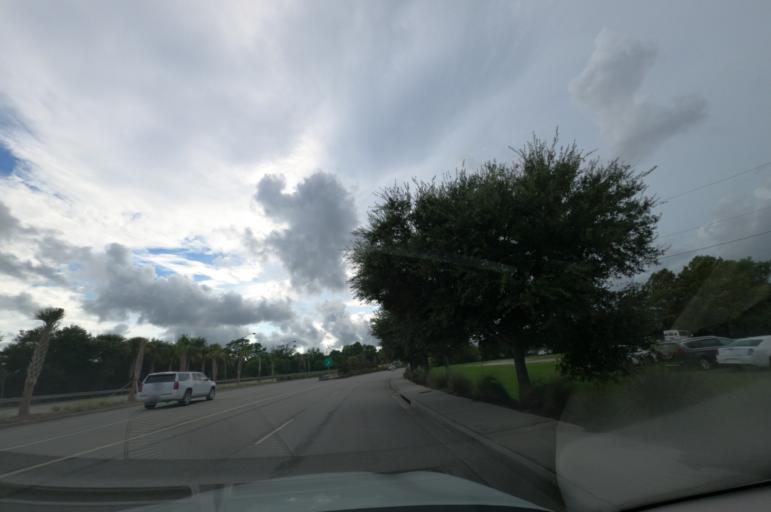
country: US
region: South Carolina
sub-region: Charleston County
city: Mount Pleasant
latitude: 32.8188
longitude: -79.8402
